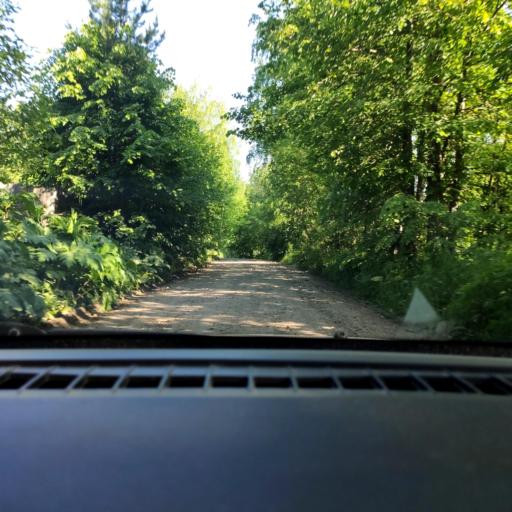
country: RU
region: Perm
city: Overyata
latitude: 58.1233
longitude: 55.8797
